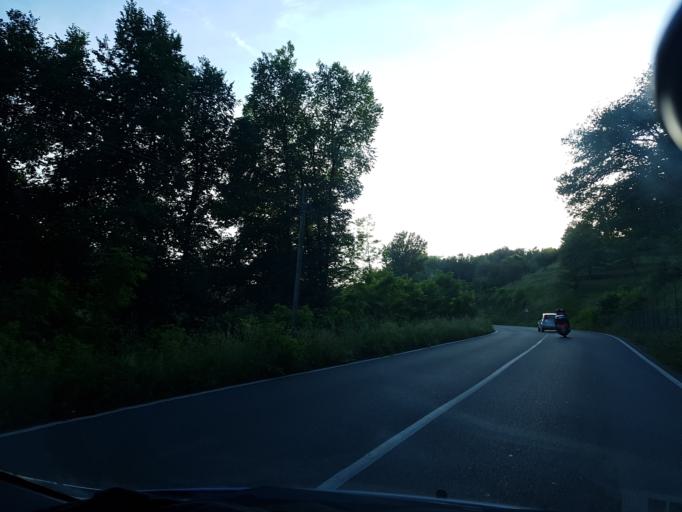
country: IT
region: Tuscany
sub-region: Provincia di Massa-Carrara
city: Fivizzano
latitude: 44.2026
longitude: 10.0852
